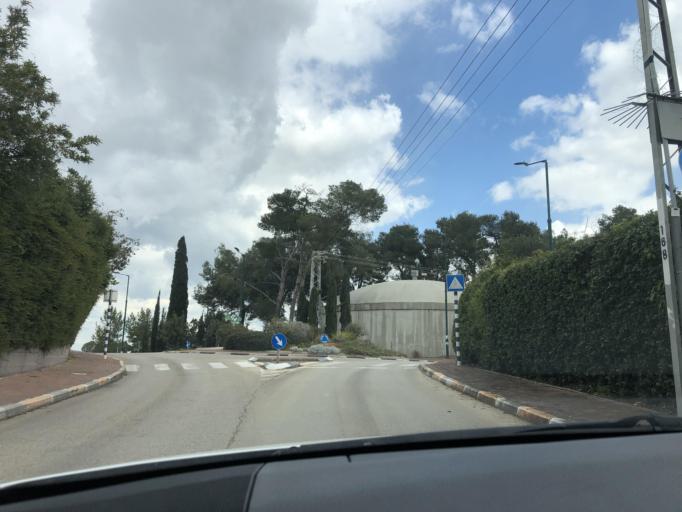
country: IL
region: Central District
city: Tel Mond
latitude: 32.2677
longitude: 34.9352
